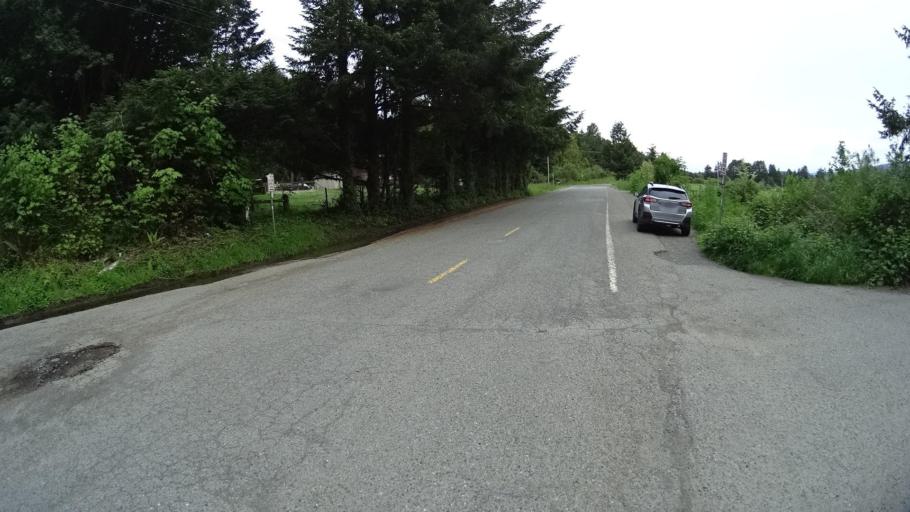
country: US
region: California
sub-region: Humboldt County
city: Blue Lake
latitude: 40.8572
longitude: -123.9945
